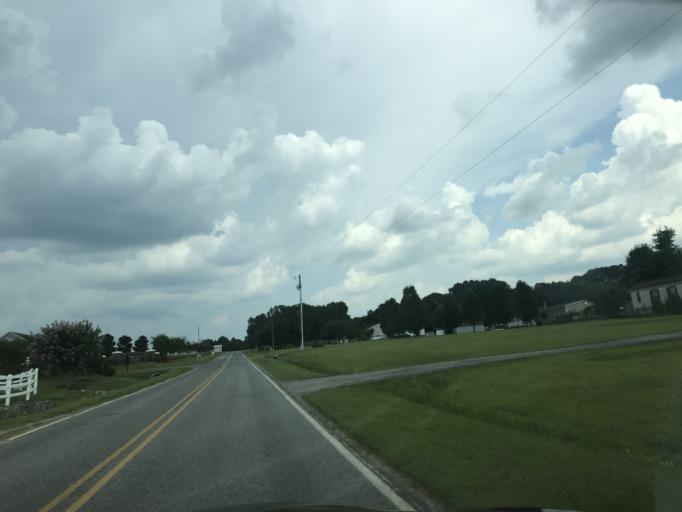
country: US
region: North Carolina
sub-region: Johnston County
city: Four Oaks
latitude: 35.5149
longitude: -78.5326
